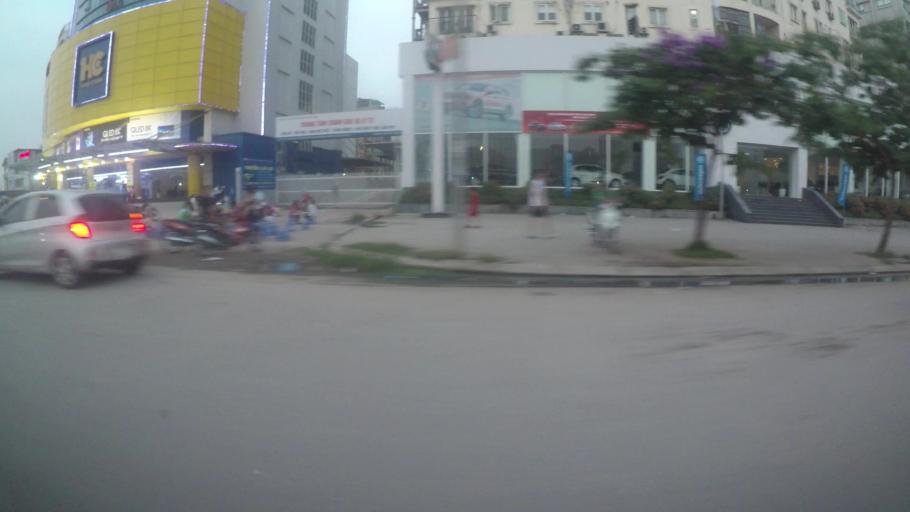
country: VN
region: Ha Noi
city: Tay Ho
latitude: 21.0687
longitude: 105.7859
